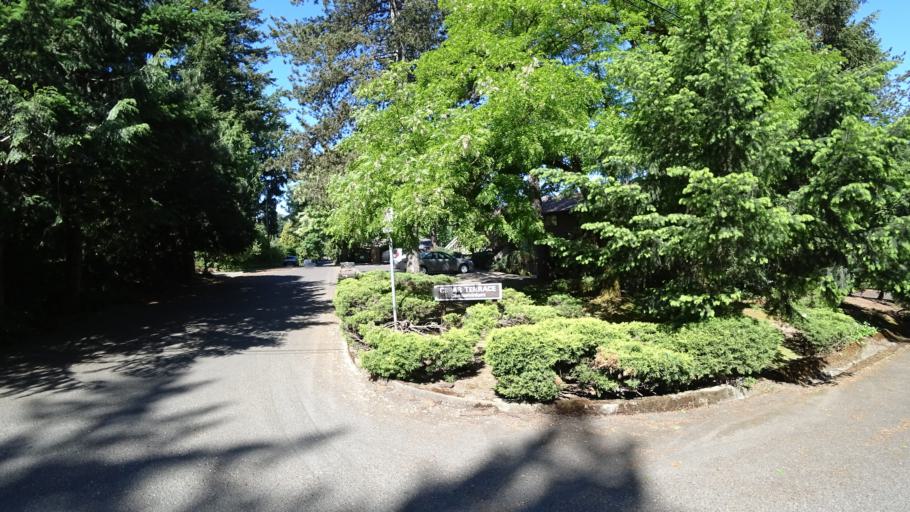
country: US
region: Oregon
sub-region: Washington County
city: Raleigh Hills
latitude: 45.4864
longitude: -122.7285
